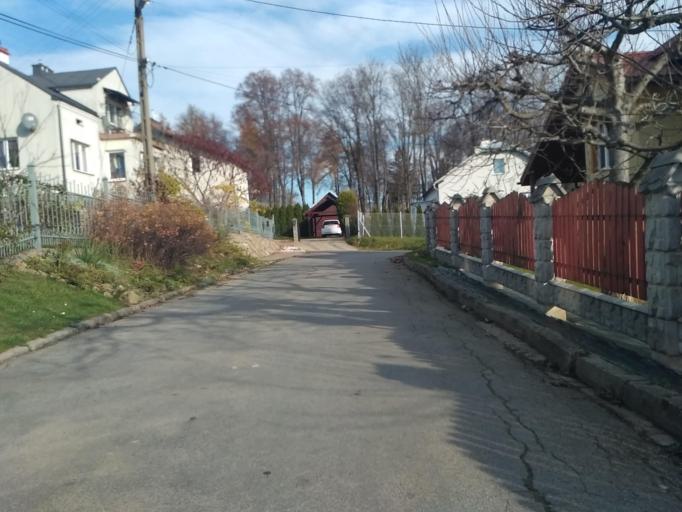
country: PL
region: Subcarpathian Voivodeship
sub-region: Powiat brzozowski
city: Brzozow
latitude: 49.6917
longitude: 22.0109
